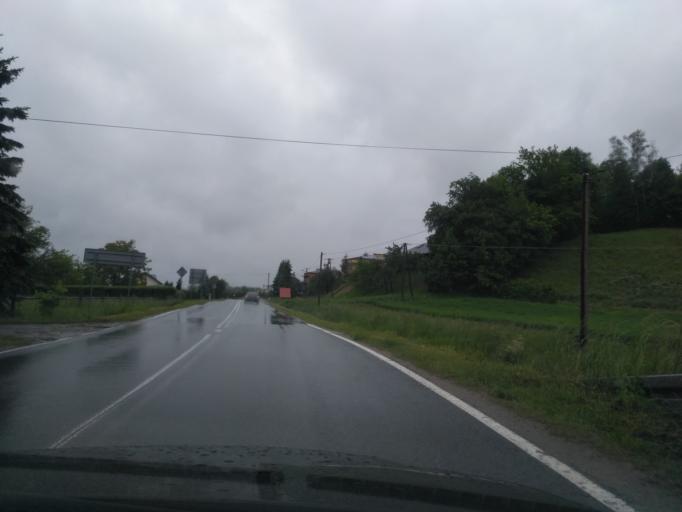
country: PL
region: Lesser Poland Voivodeship
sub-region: Powiat gorlicki
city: Sekowa
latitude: 49.6230
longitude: 21.1979
